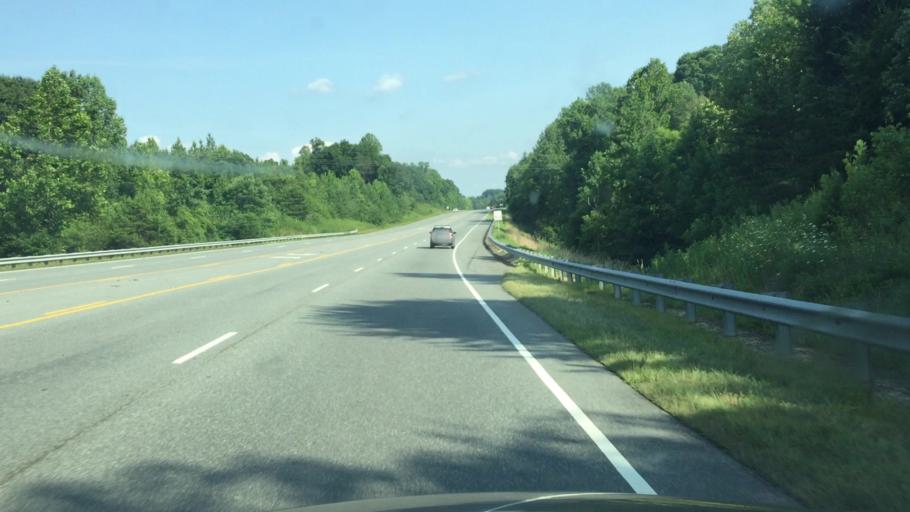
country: US
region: North Carolina
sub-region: Rockingham County
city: Reidsville
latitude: 36.3722
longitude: -79.6482
